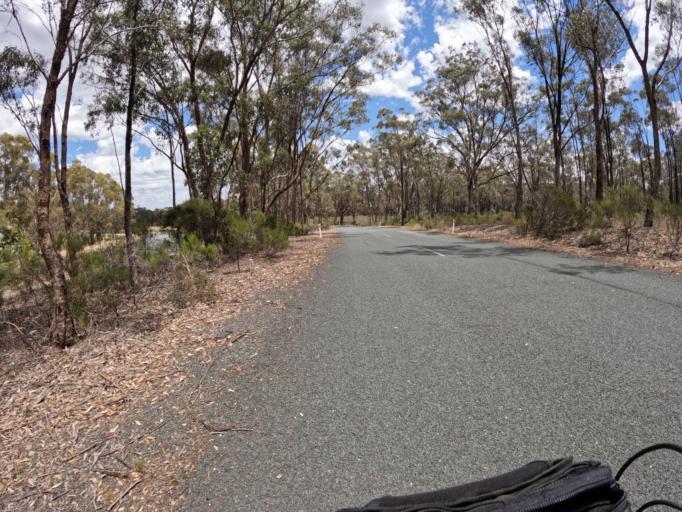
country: AU
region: Victoria
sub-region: Greater Shepparton
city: Shepparton
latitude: -36.6848
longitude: 145.1827
